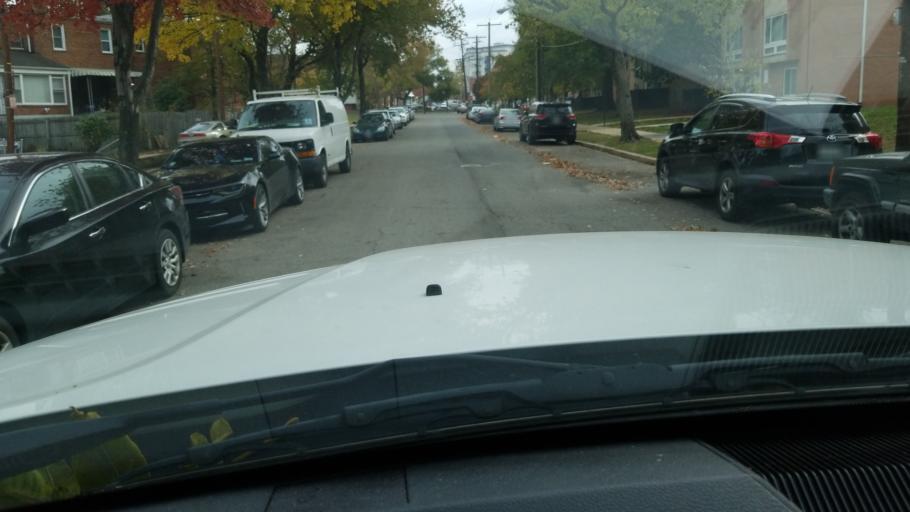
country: US
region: Maryland
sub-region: Prince George's County
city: Capitol Heights
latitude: 38.8919
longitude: -76.9417
